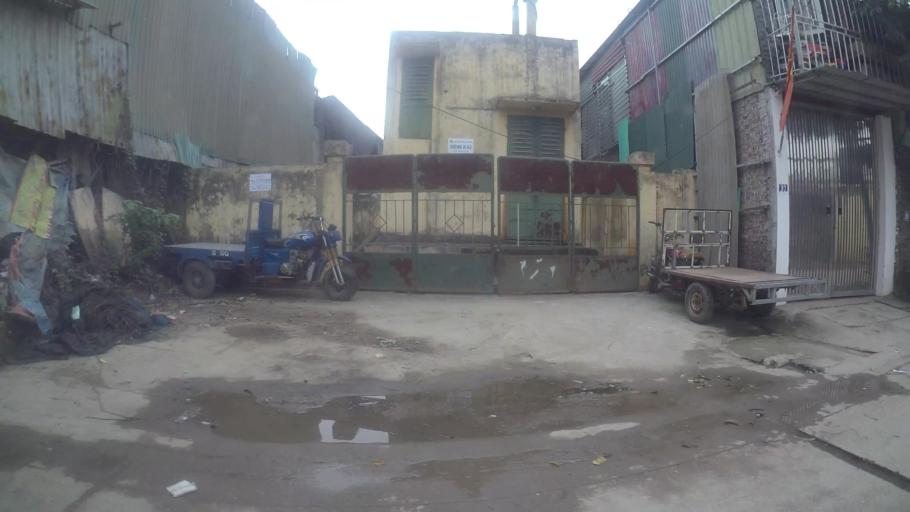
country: VN
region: Ha Noi
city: Tay Ho
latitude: 21.0696
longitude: 105.8281
